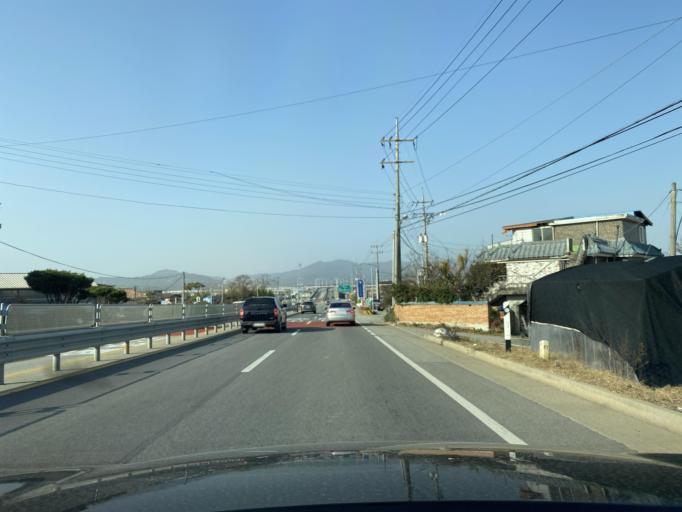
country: KR
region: Chungcheongnam-do
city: Yesan
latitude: 36.6904
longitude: 126.7458
